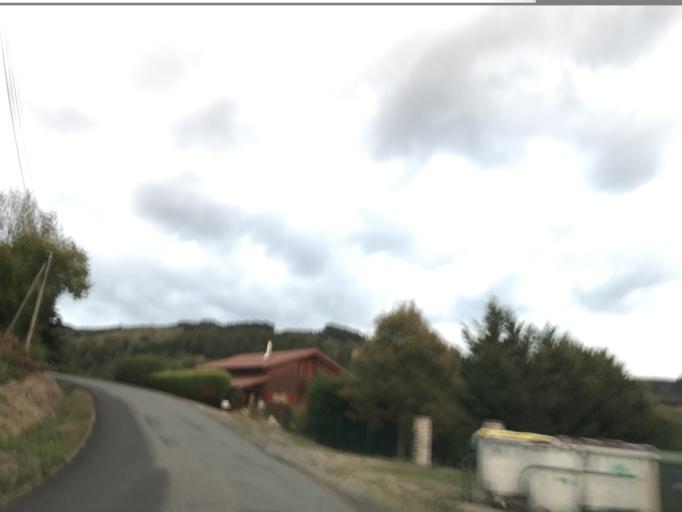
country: FR
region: Auvergne
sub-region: Departement du Puy-de-Dome
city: Escoutoux
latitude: 45.8257
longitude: 3.5636
